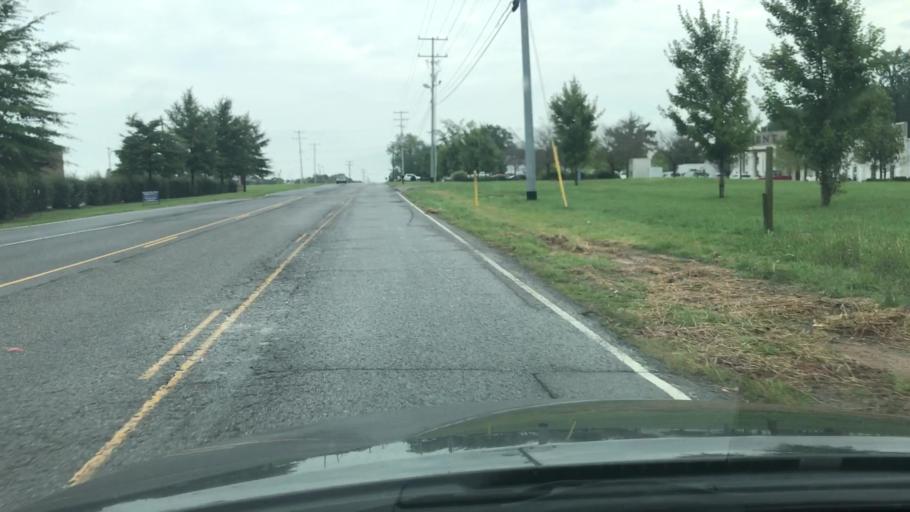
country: US
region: Tennessee
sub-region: Sumner County
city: White House
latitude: 36.4617
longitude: -86.6754
